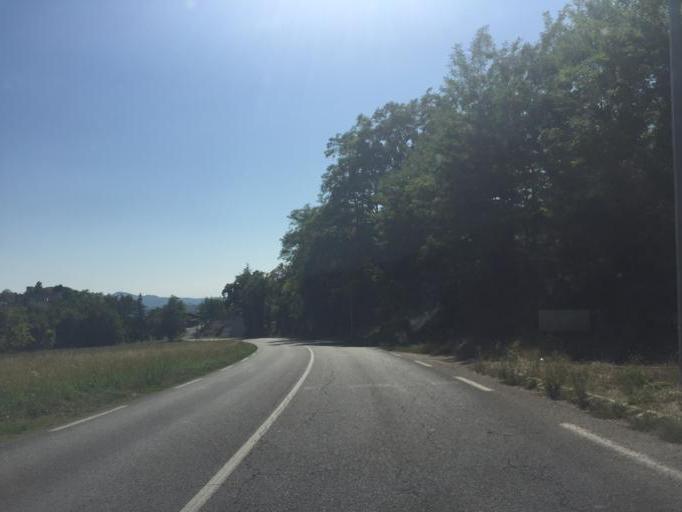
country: FR
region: Provence-Alpes-Cote d'Azur
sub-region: Departement des Alpes-de-Haute-Provence
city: Mane
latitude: 43.9433
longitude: 5.7707
